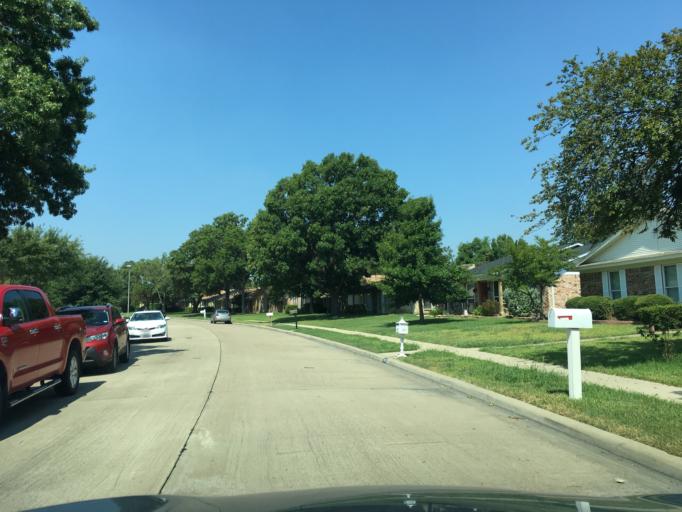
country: US
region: Texas
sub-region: Dallas County
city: Garland
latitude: 32.9346
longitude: -96.6499
